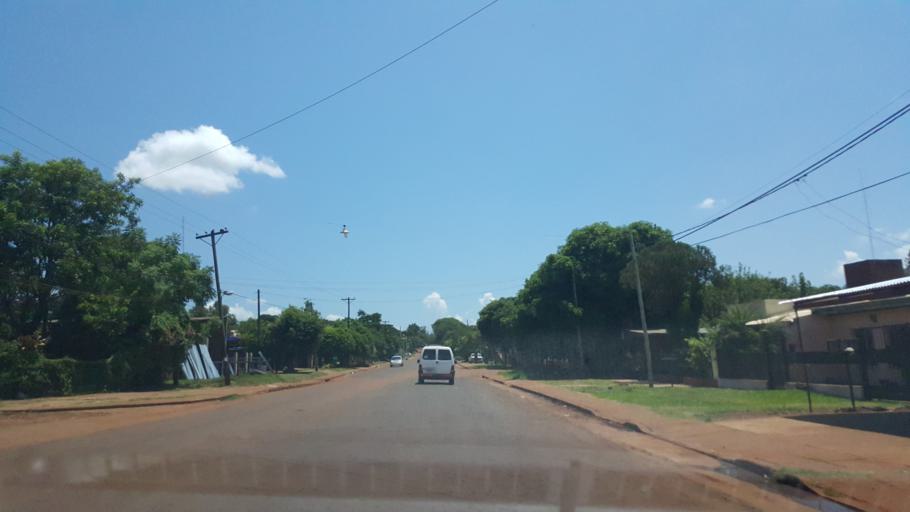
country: AR
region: Misiones
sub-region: Departamento de Capital
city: Posadas
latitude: -27.4064
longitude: -55.9166
